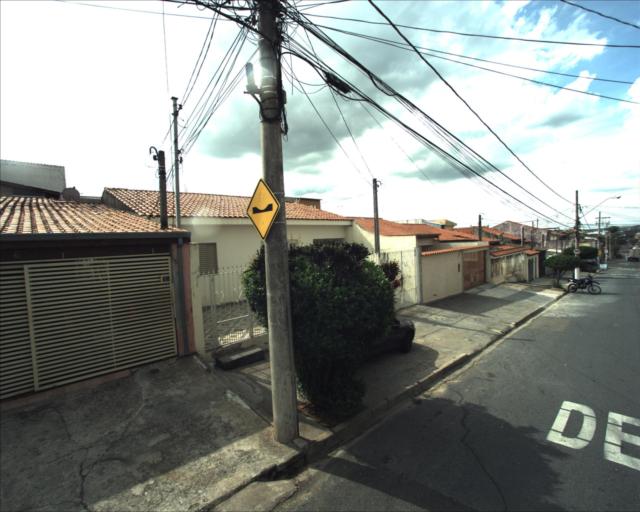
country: BR
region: Sao Paulo
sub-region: Sorocaba
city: Sorocaba
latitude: -23.4647
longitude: -47.4718
